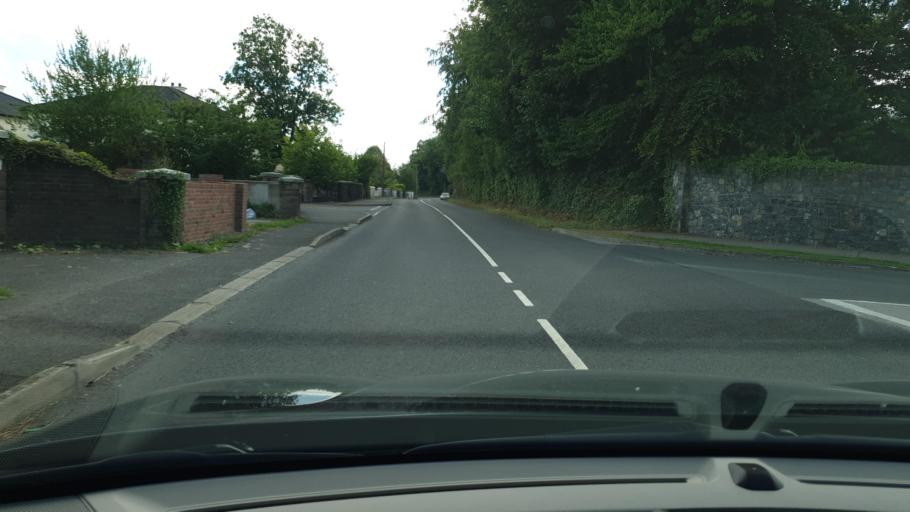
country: IE
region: Leinster
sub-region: An Mhi
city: Dunboyne
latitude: 53.4141
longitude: -6.4732
